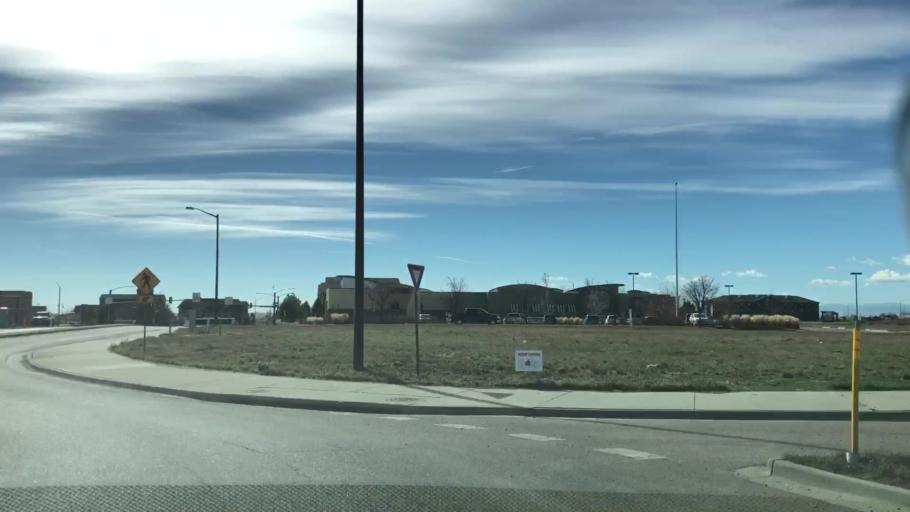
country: US
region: Colorado
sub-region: Weld County
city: Windsor
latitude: 40.4378
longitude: -104.9882
